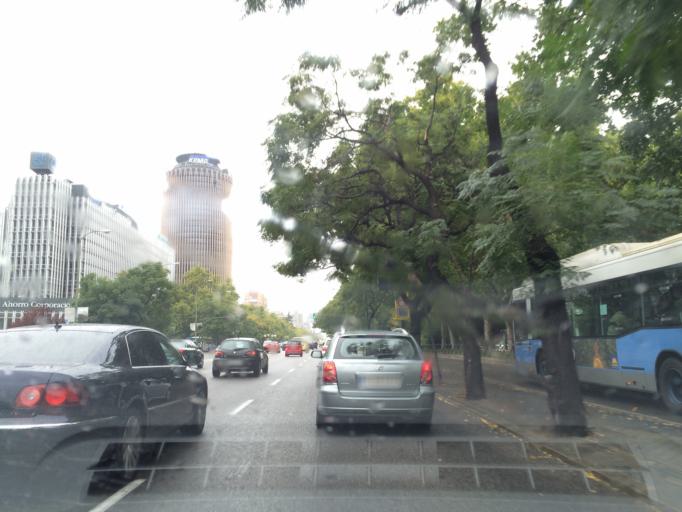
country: ES
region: Madrid
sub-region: Provincia de Madrid
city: Chamberi
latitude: 40.4482
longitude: -3.6909
